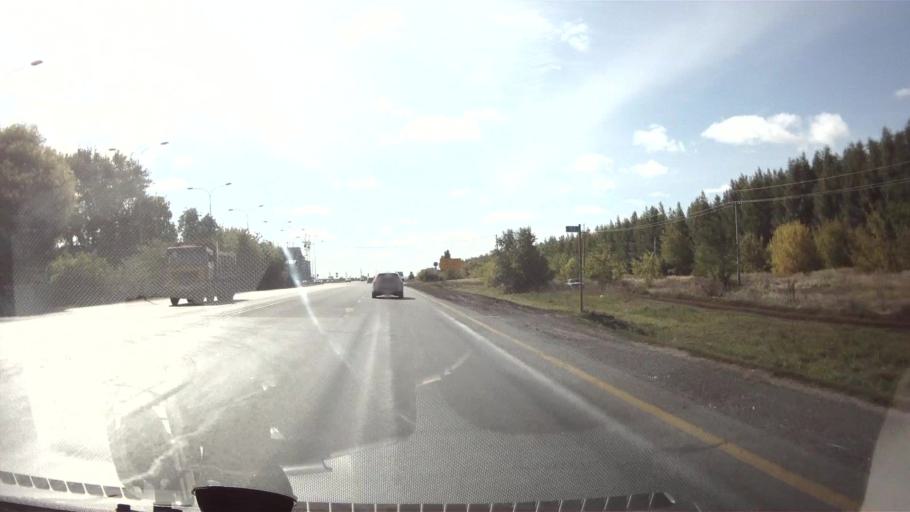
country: RU
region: Ulyanovsk
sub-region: Ulyanovskiy Rayon
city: Ulyanovsk
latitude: 54.2879
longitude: 48.2558
